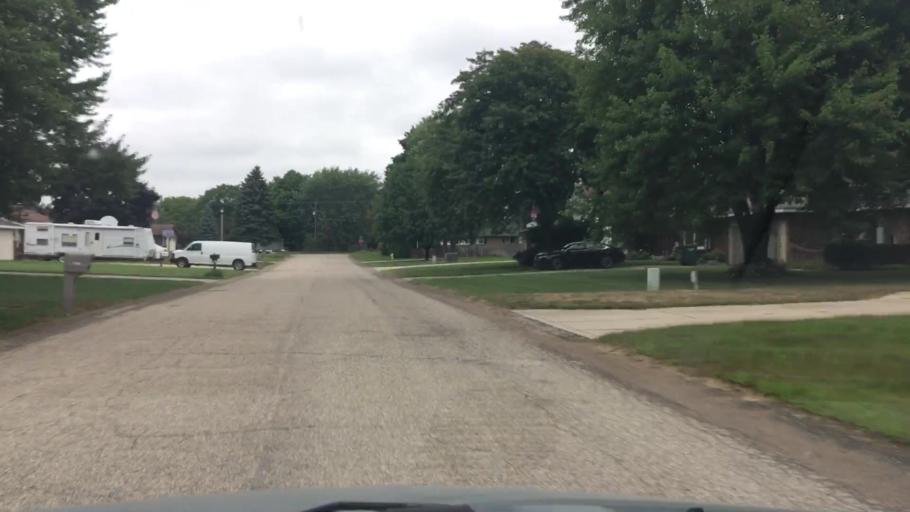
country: US
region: Michigan
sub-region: Ottawa County
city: Hudsonville
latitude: 42.9057
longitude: -85.8453
